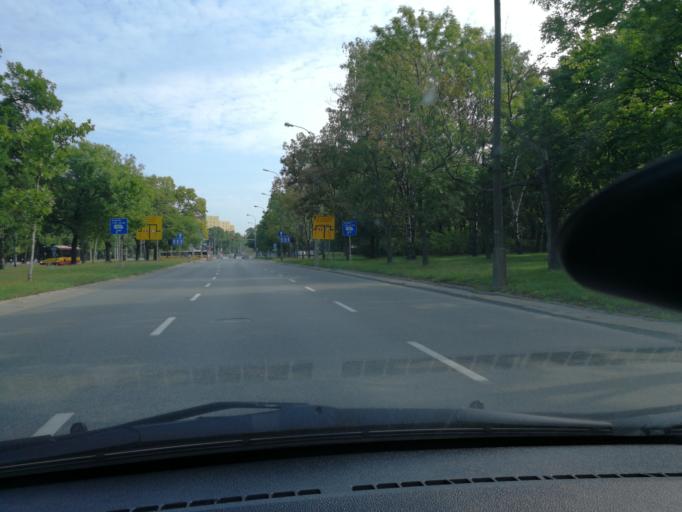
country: PL
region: Masovian Voivodeship
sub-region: Warszawa
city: Ochota
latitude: 52.2280
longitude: 20.9481
